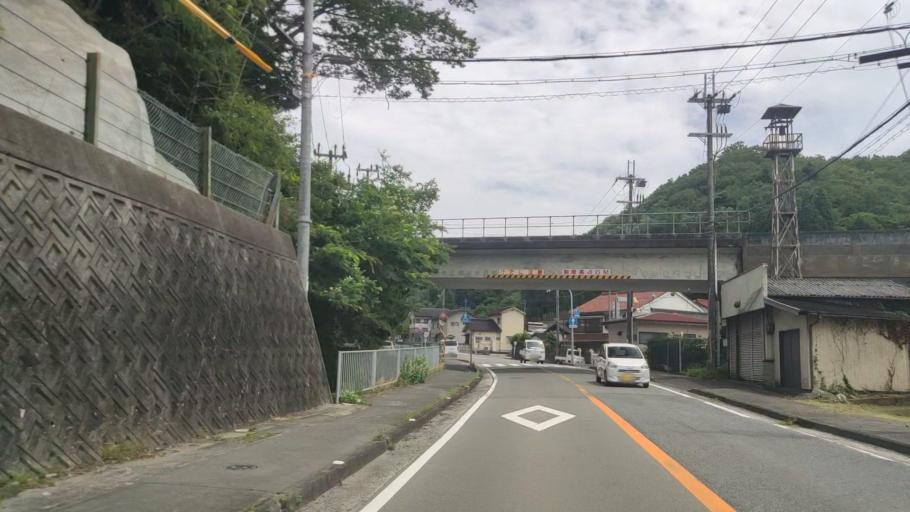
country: JP
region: Hyogo
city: Yamazakicho-nakabirose
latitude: 35.0058
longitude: 134.3639
